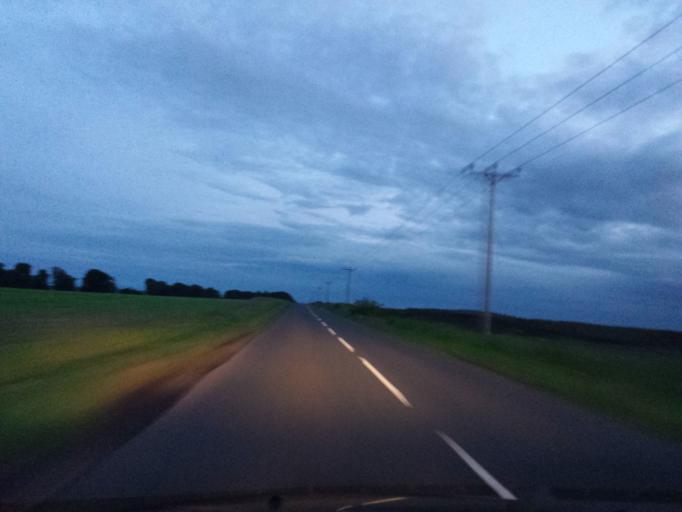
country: GB
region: Scotland
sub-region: The Scottish Borders
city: Duns
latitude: 55.7237
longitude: -2.4524
